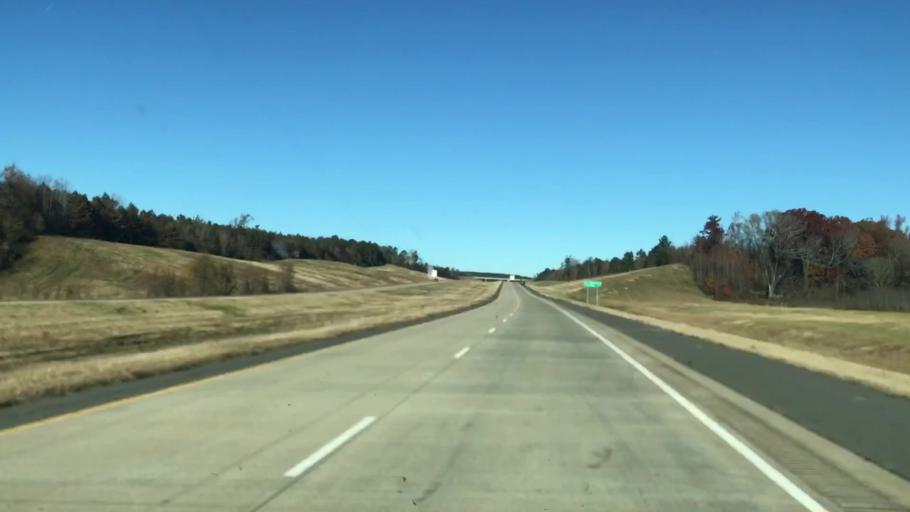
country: US
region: Louisiana
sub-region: Caddo Parish
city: Vivian
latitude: 32.9109
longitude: -93.8710
